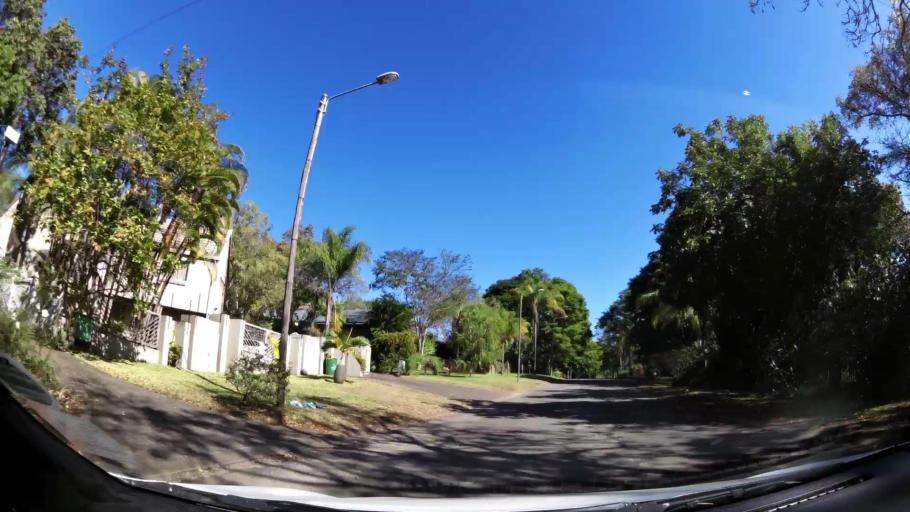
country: ZA
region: Limpopo
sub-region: Mopani District Municipality
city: Tzaneen
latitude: -23.8335
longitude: 30.1495
